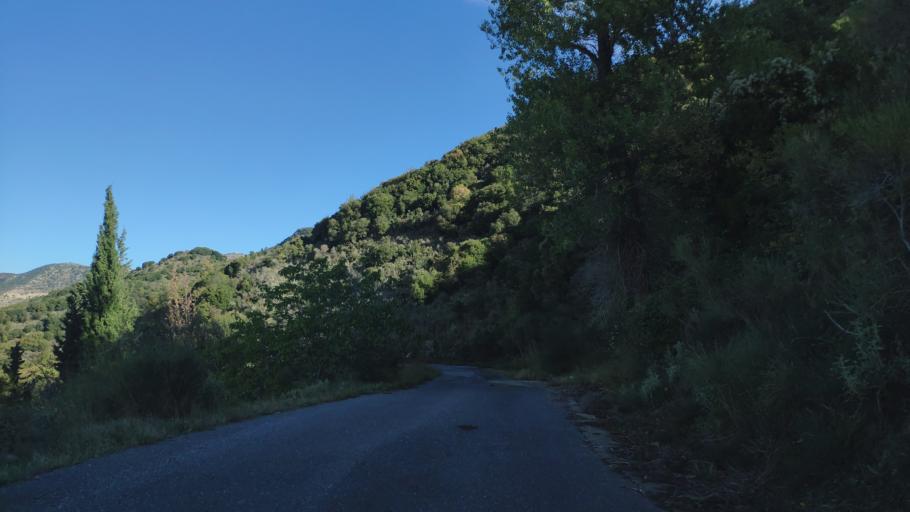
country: GR
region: Peloponnese
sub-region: Nomos Arkadias
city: Dimitsana
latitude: 37.5538
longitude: 22.0605
